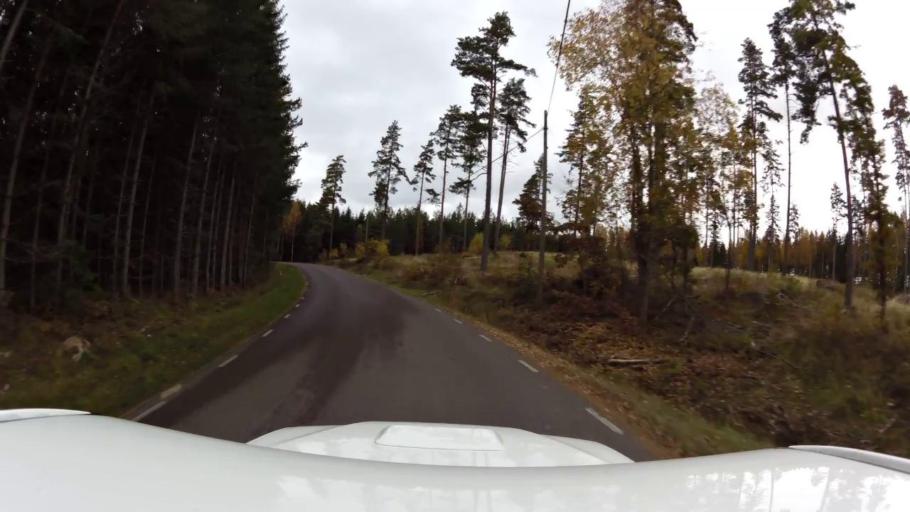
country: SE
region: OEstergoetland
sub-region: Linkopings Kommun
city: Ljungsbro
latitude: 58.5595
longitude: 15.3980
